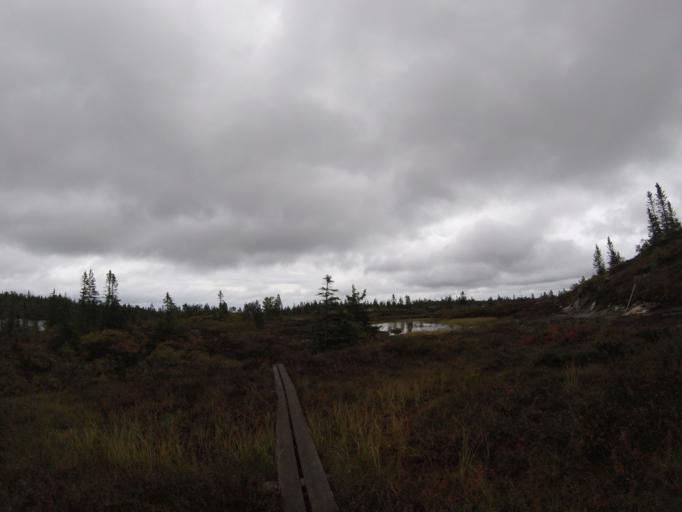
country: NO
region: Buskerud
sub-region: Flesberg
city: Lampeland
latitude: 59.7744
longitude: 9.4021
